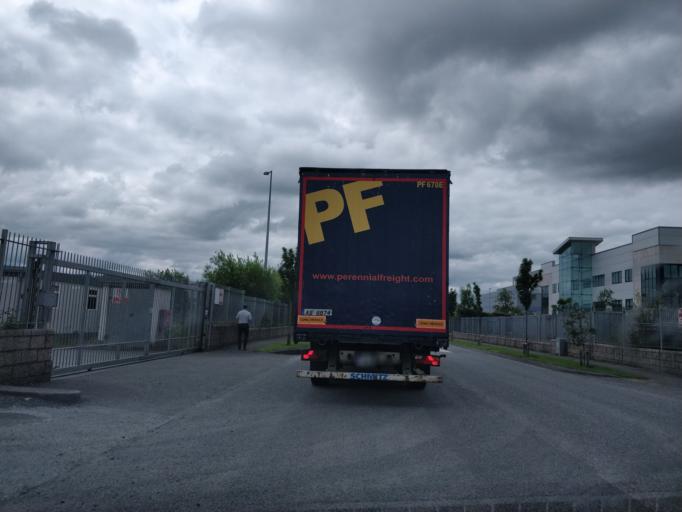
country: IE
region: Leinster
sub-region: South Dublin
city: Rathcoole
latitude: 53.2974
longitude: -6.4646
